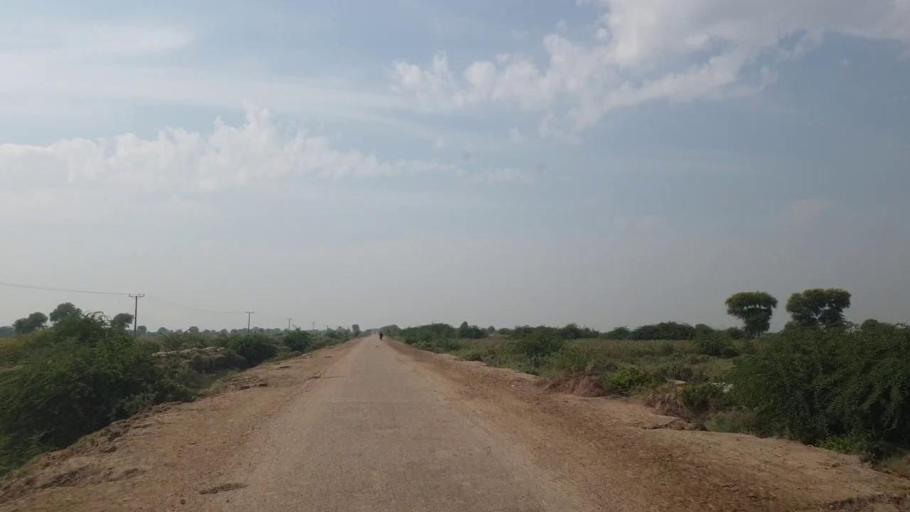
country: PK
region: Sindh
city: Rajo Khanani
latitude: 24.9689
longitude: 69.0177
